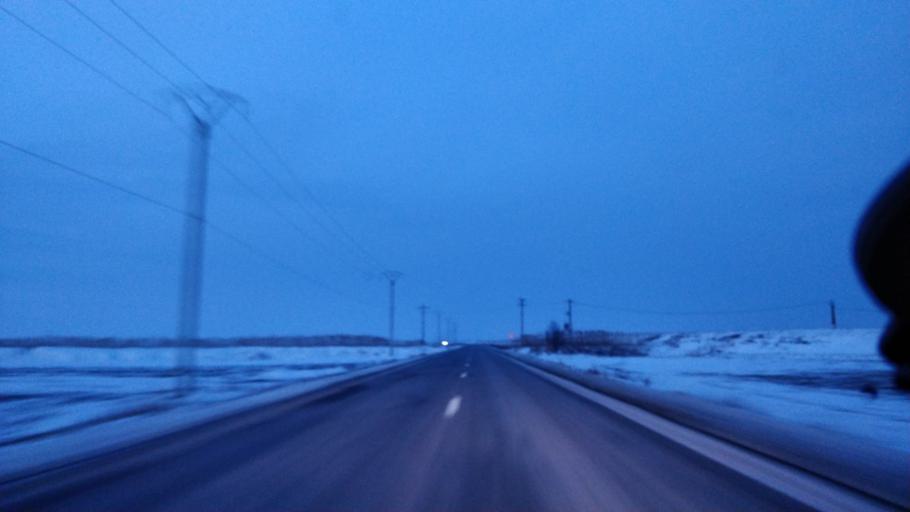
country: RO
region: Vrancea
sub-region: Comuna Nanesti
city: Nanesti
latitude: 45.5589
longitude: 27.4998
